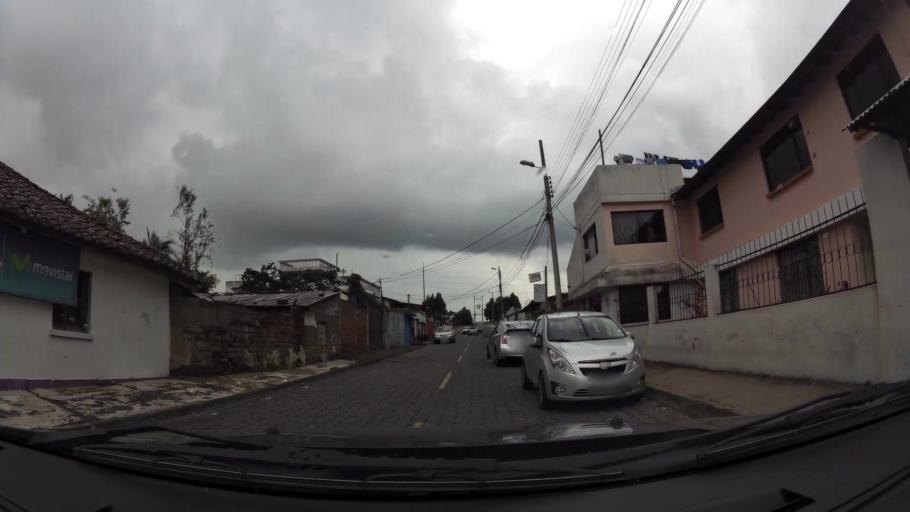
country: EC
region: Pichincha
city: Sangolqui
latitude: -0.3135
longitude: -78.4587
